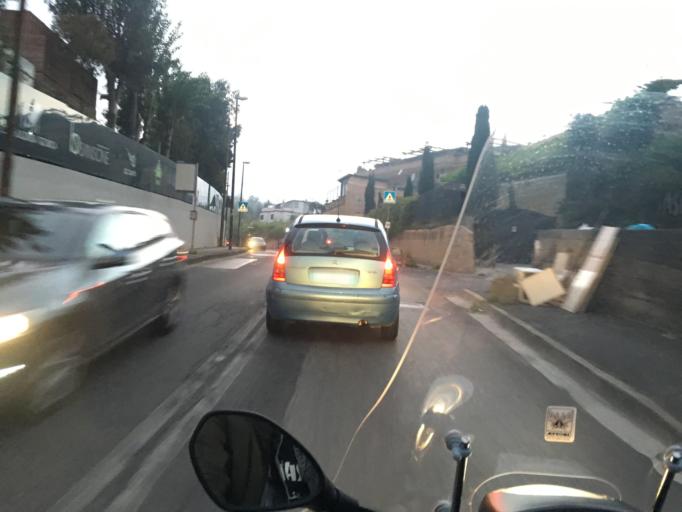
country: IT
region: Campania
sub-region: Provincia di Napoli
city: Torre Caracciolo
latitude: 40.8631
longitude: 14.2110
